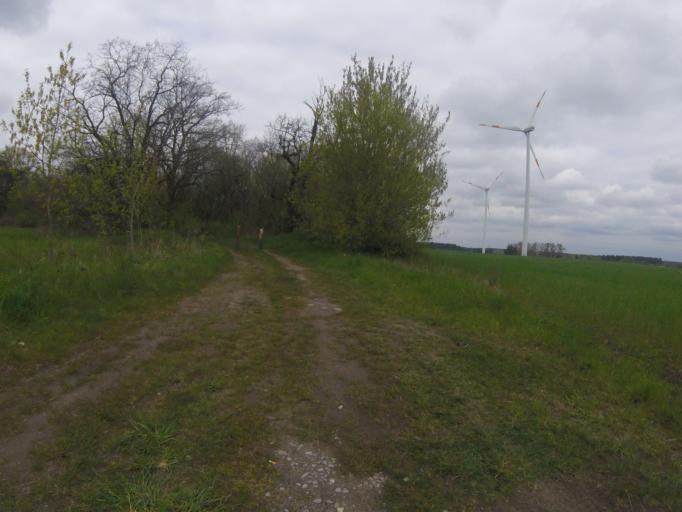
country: DE
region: Brandenburg
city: Mittenwalde
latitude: 52.2475
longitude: 13.5842
